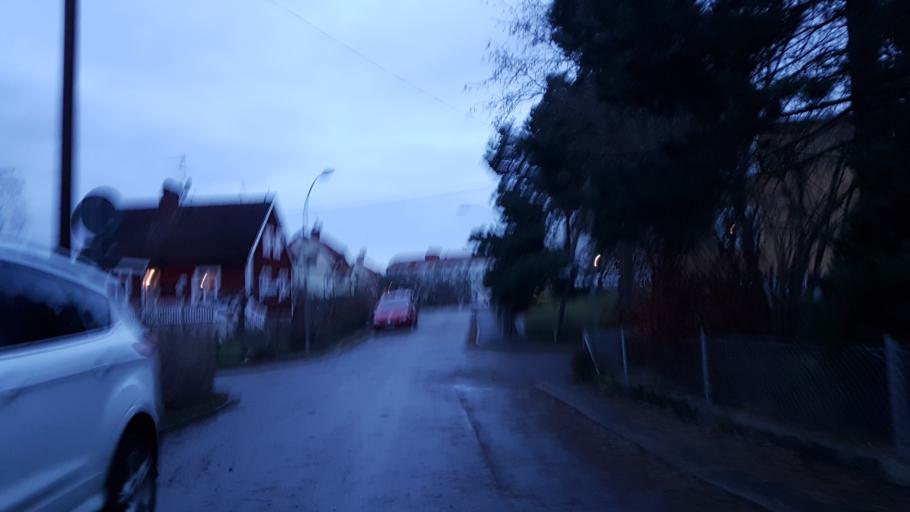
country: SE
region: Stockholm
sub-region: Stockholms Kommun
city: Arsta
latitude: 59.2763
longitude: 18.0516
